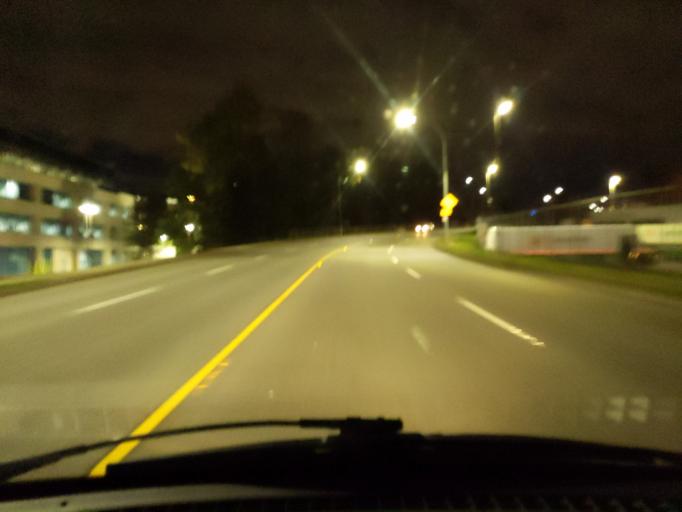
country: CA
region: British Columbia
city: Burnaby
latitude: 49.2594
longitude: -123.0128
